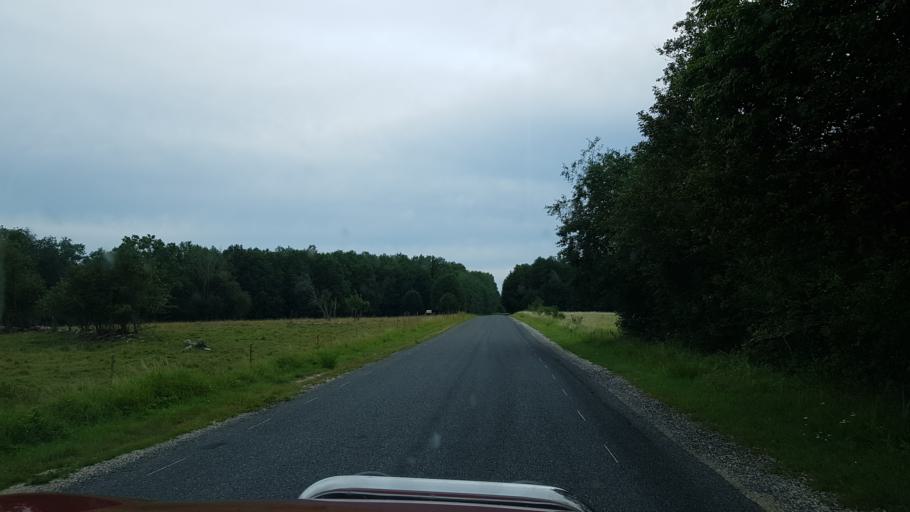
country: EE
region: Laeaene
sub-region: Lihula vald
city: Lihula
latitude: 58.8625
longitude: 23.8265
